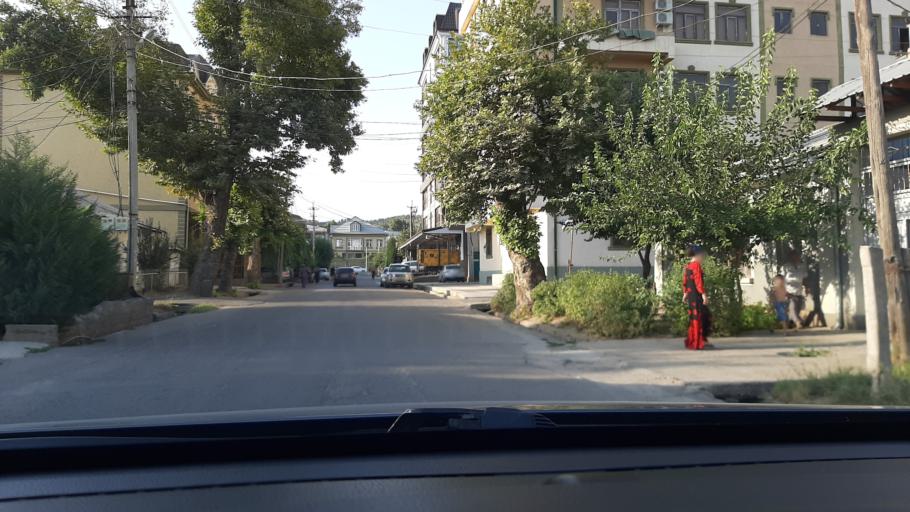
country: TJ
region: Dushanbe
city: Dushanbe
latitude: 38.5661
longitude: 68.8118
